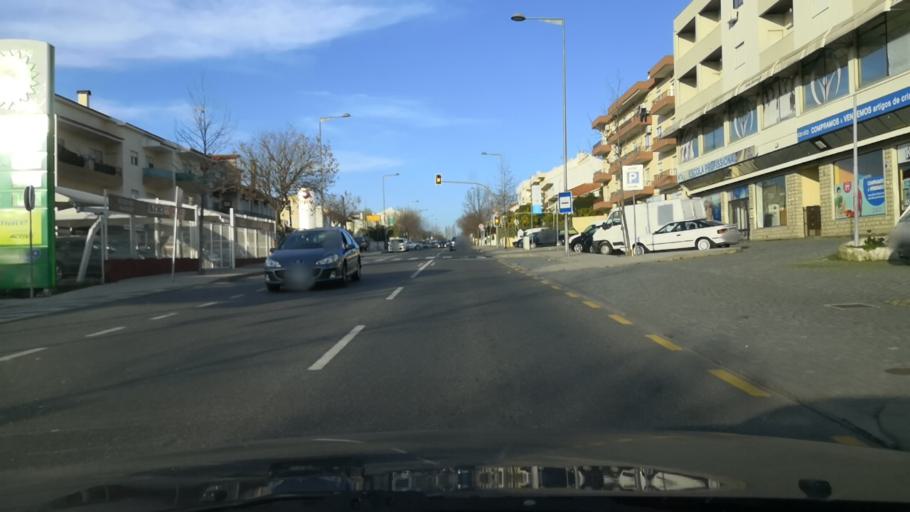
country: PT
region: Castelo Branco
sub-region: Castelo Branco
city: Castelo Branco
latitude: 39.8083
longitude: -7.5110
